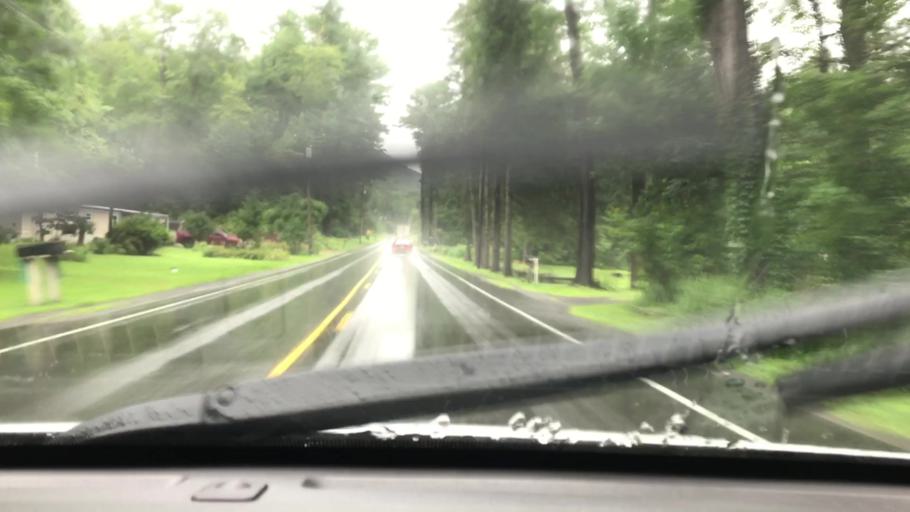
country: US
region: Pennsylvania
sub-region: Blair County
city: Tyrone
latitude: 40.7494
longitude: -78.2138
